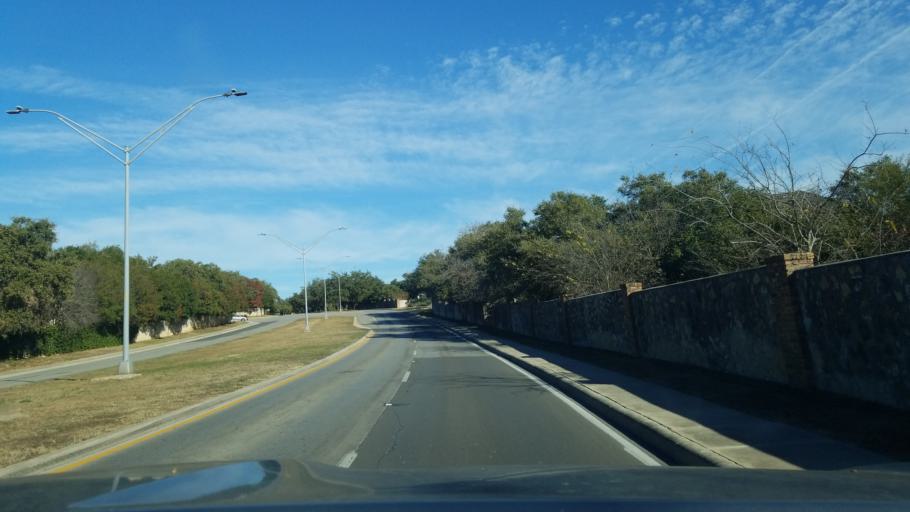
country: US
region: Texas
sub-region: Bexar County
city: Hollywood Park
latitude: 29.6030
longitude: -98.5219
